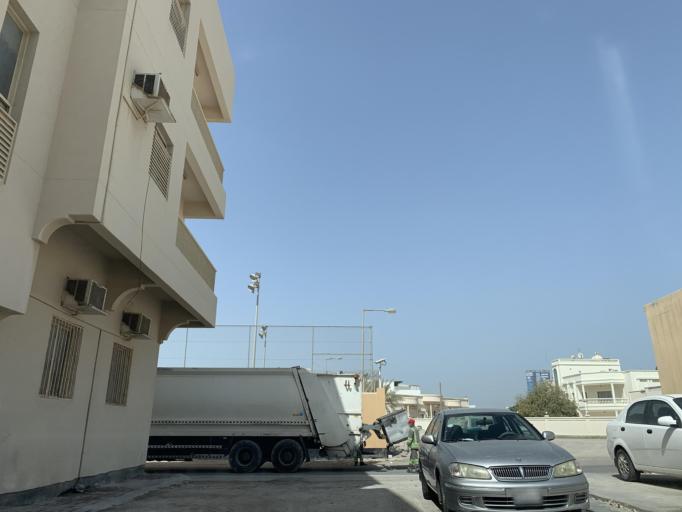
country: BH
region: Northern
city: Sitrah
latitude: 26.1466
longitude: 50.6010
